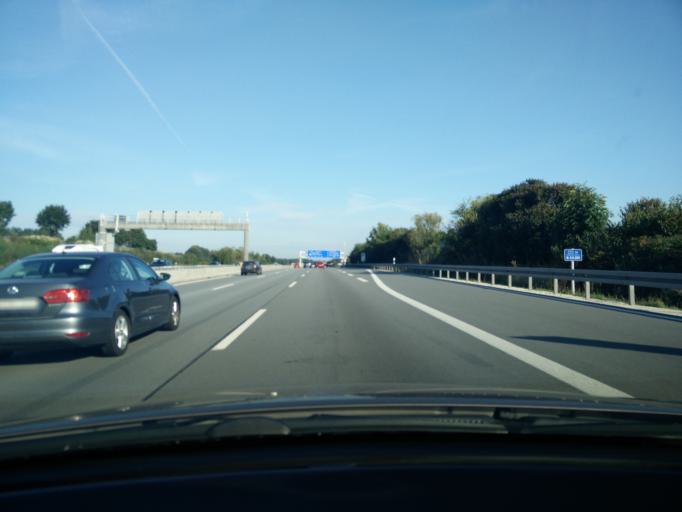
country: DE
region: Bavaria
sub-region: Upper Bavaria
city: Schweitenkirchen
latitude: 48.5018
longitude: 11.5922
